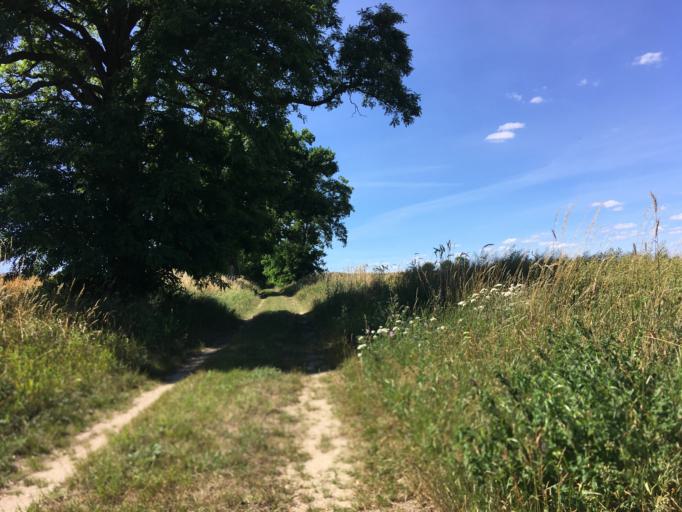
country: DE
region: Brandenburg
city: Brussow
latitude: 53.3287
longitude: 14.0756
